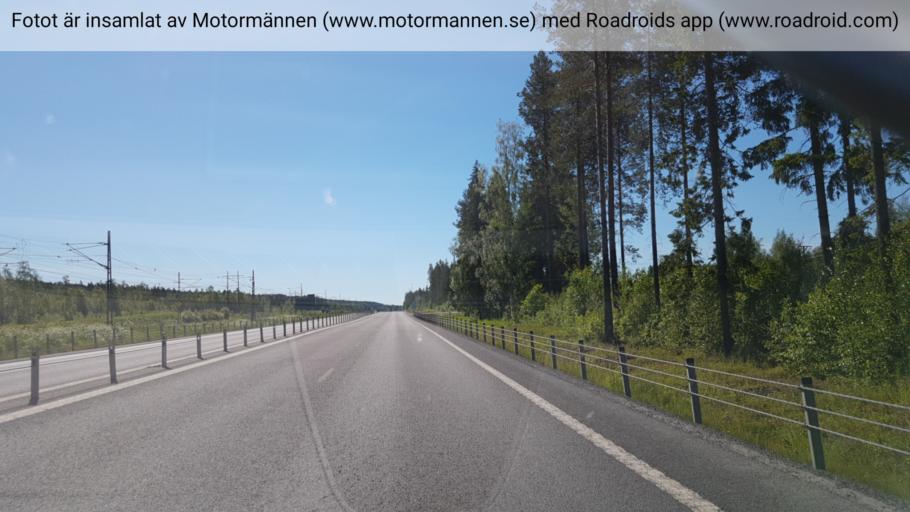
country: SE
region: Norrbotten
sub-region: Bodens Kommun
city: Saevast
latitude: 65.7797
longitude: 21.7445
